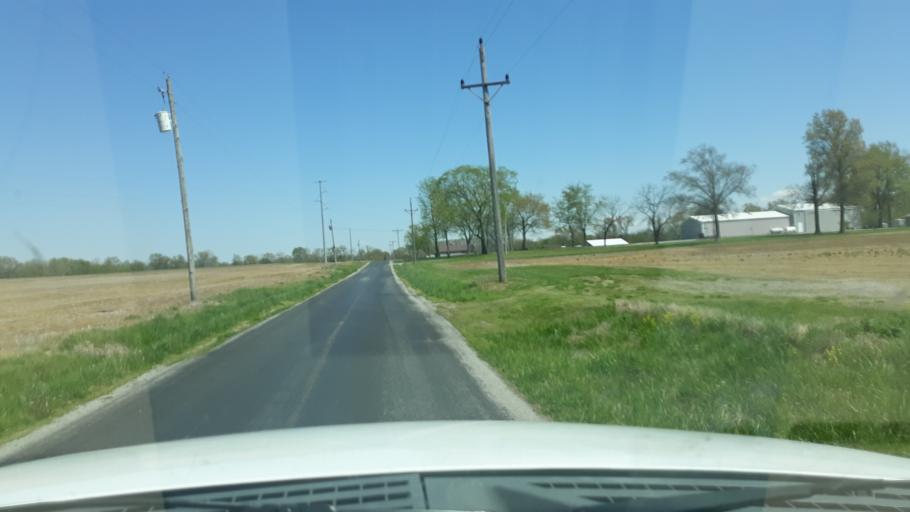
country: US
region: Illinois
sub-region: Saline County
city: Harrisburg
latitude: 37.8341
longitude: -88.6279
